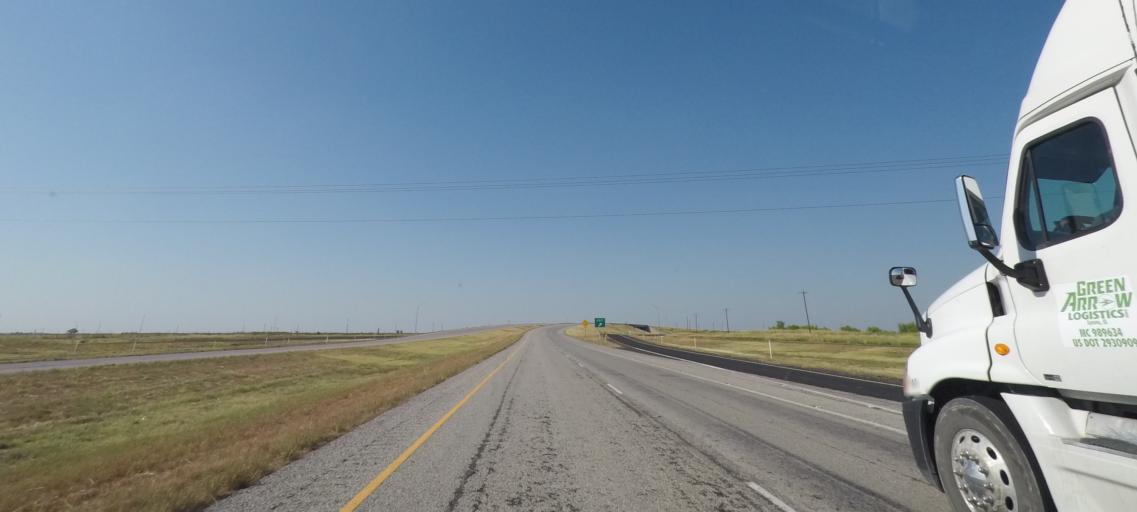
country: US
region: Texas
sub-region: Baylor County
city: Seymour
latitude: 33.6106
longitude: -99.2429
